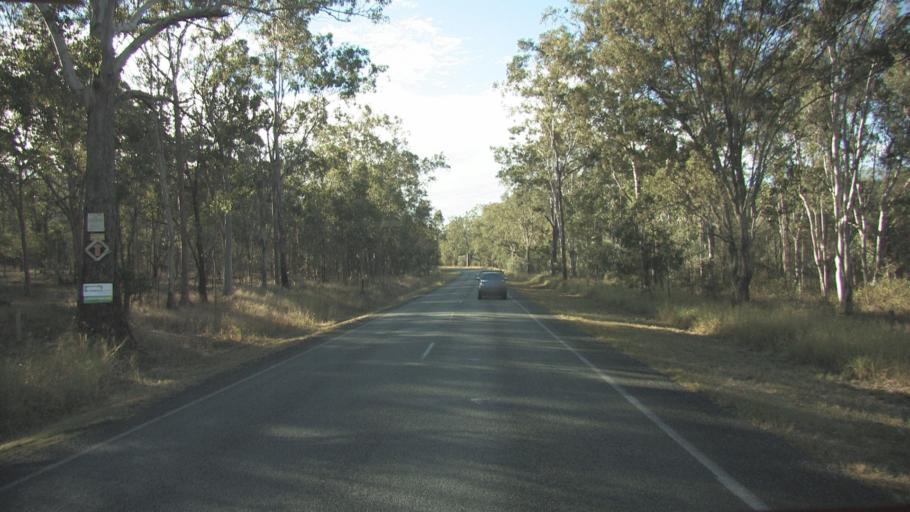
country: AU
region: Queensland
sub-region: Logan
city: Cedar Vale
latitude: -27.9045
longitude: 153.0905
